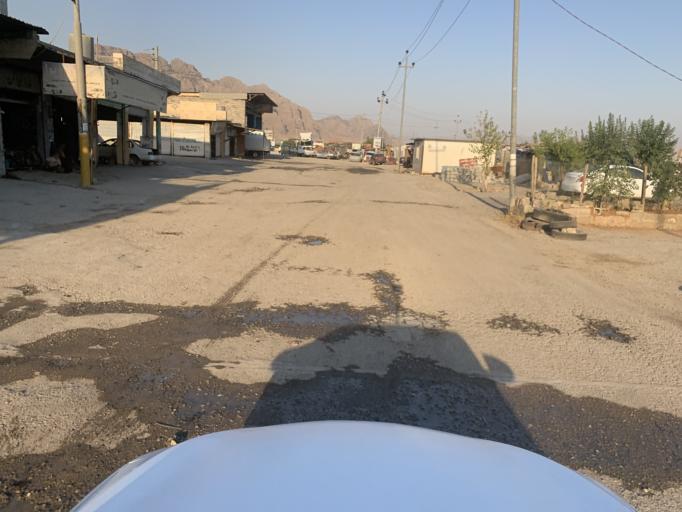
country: IQ
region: As Sulaymaniyah
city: Raniye
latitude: 36.2446
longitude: 44.8877
